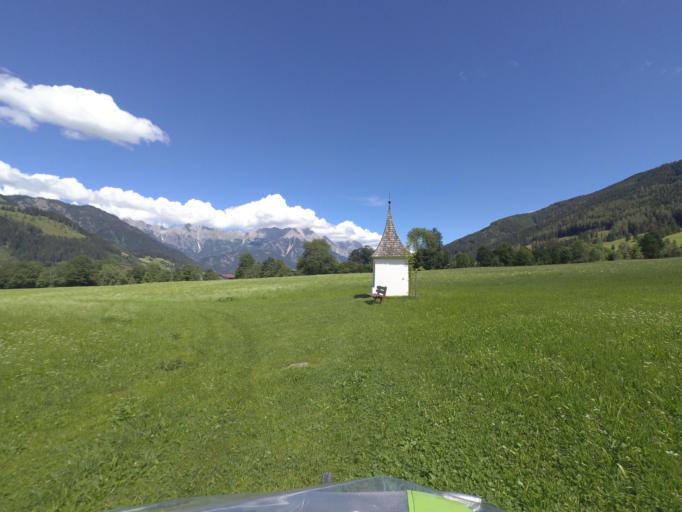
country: AT
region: Salzburg
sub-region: Politischer Bezirk Zell am See
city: Leogang
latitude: 47.4362
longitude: 12.7631
